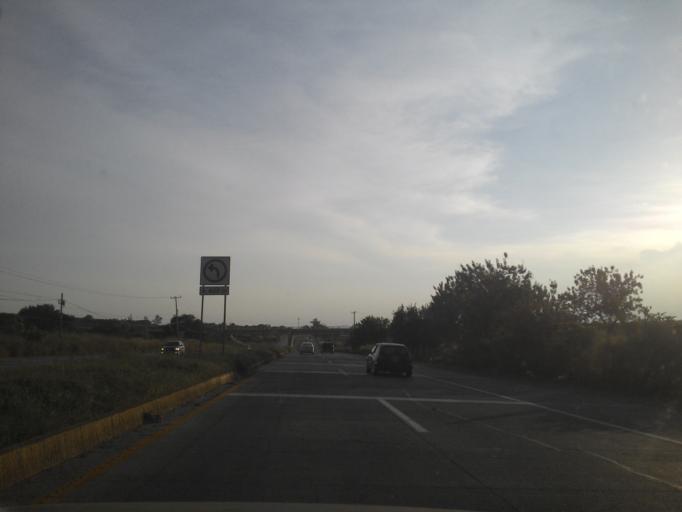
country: MX
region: Jalisco
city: Zapotlanejo
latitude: 20.6007
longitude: -103.0992
